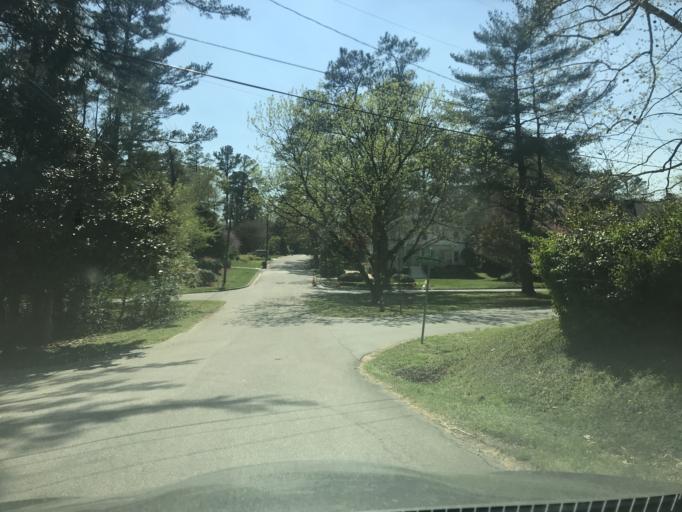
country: US
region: North Carolina
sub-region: Wake County
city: West Raleigh
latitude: 35.8152
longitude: -78.6392
